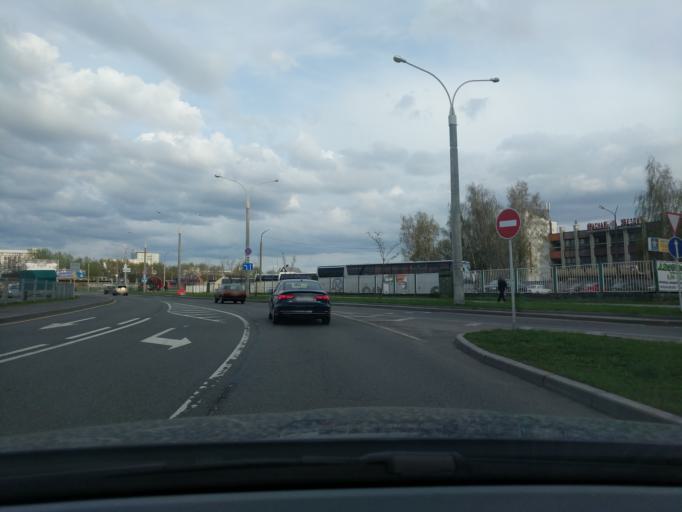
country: BY
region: Minsk
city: Minsk
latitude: 53.9064
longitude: 27.5218
